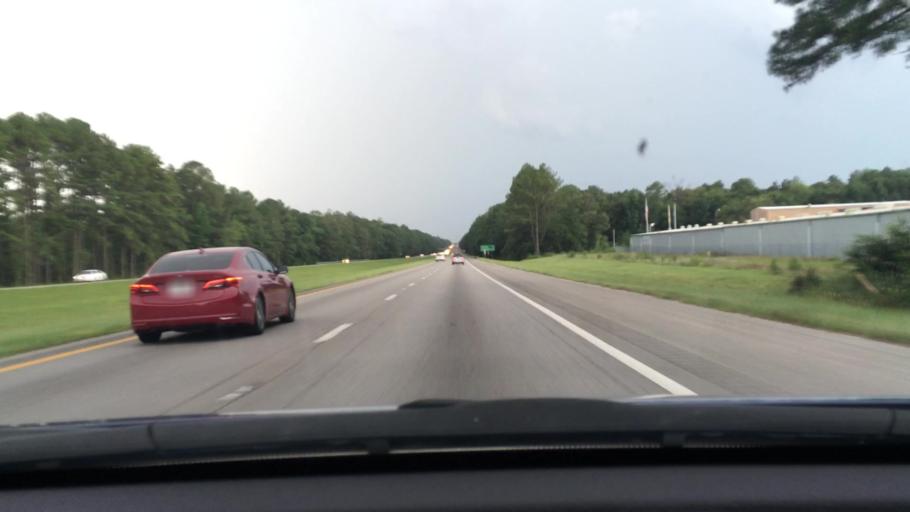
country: US
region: South Carolina
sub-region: Kershaw County
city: Elgin
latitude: 34.1362
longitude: -80.7615
